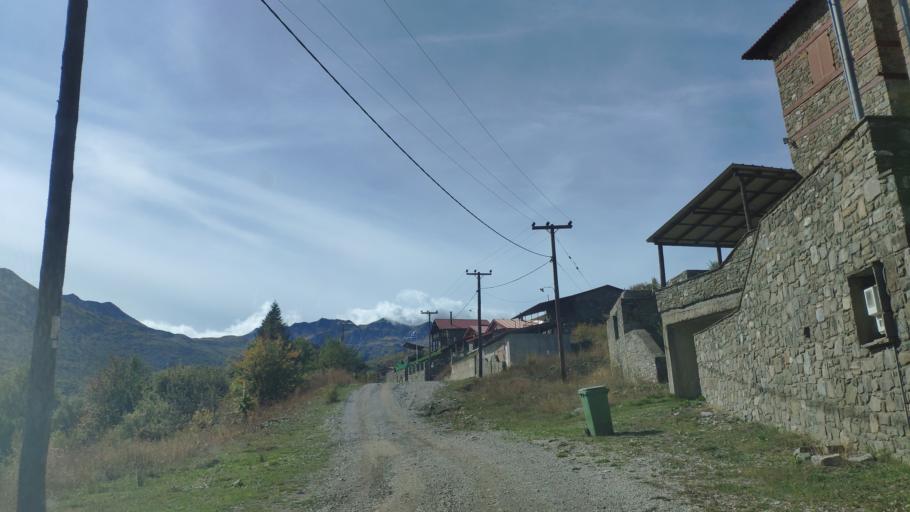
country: AL
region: Korce
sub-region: Rrethi i Devollit
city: Miras
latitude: 40.3945
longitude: 20.8365
